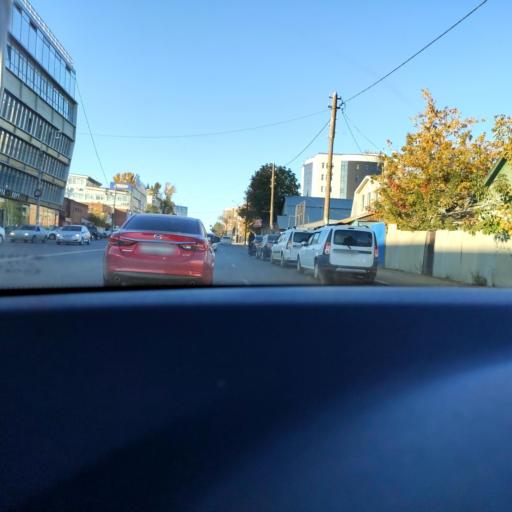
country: RU
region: Samara
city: Samara
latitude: 53.1979
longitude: 50.1905
